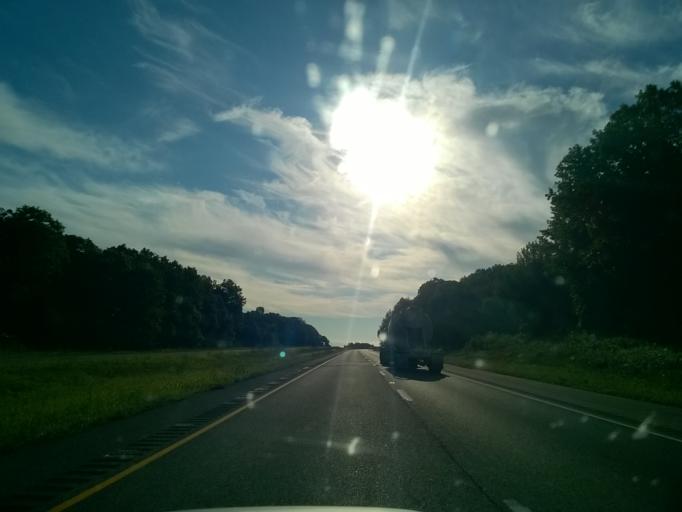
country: US
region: Indiana
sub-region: Warrick County
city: Boonville
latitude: 38.1997
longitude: -87.1875
